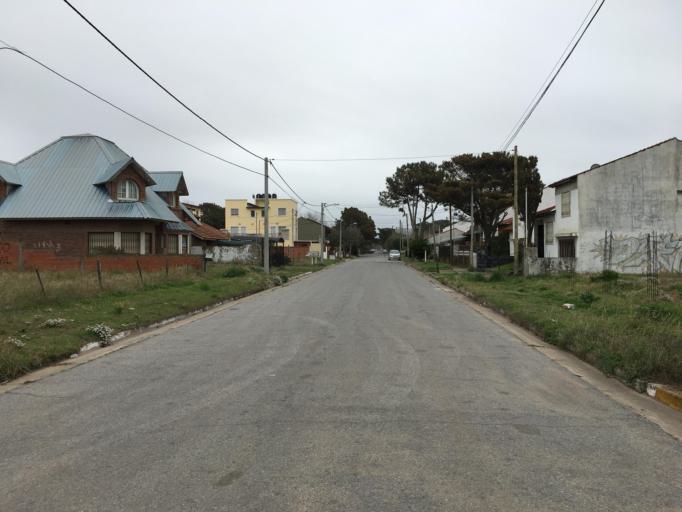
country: AR
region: Buenos Aires
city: Mar del Tuyu
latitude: -36.5547
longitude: -56.6898
